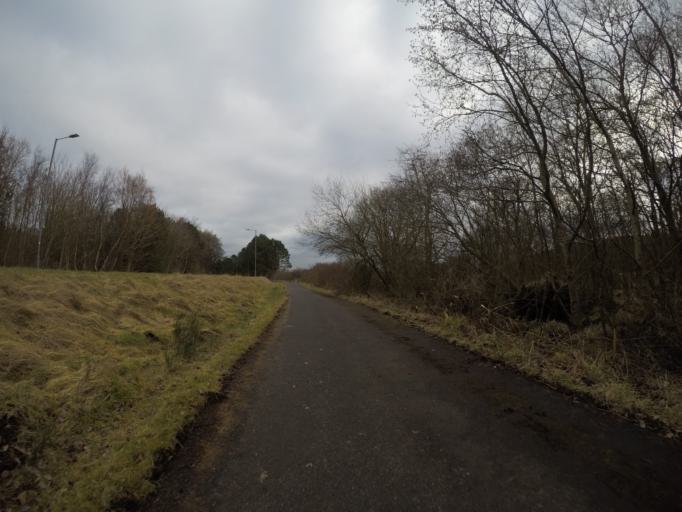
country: GB
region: Scotland
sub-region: North Ayrshire
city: Irvine
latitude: 55.5903
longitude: -4.6587
